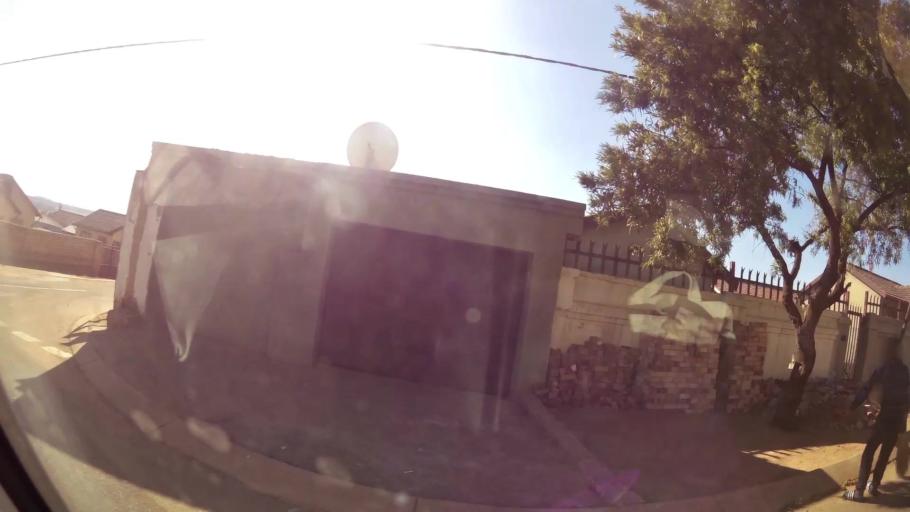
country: ZA
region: Gauteng
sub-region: City of Tshwane Metropolitan Municipality
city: Cullinan
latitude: -25.6907
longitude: 28.4120
